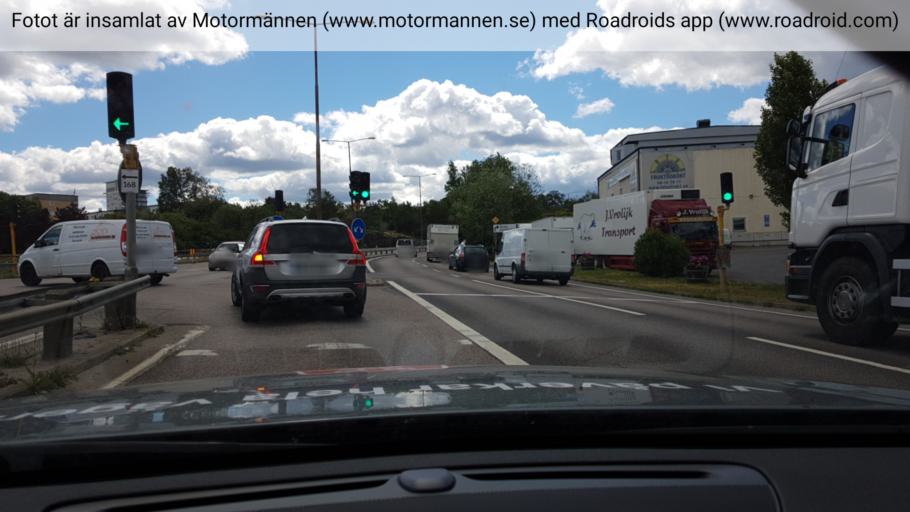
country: SE
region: Stockholm
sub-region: Stockholms Kommun
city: Arsta
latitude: 59.2931
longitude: 18.0335
